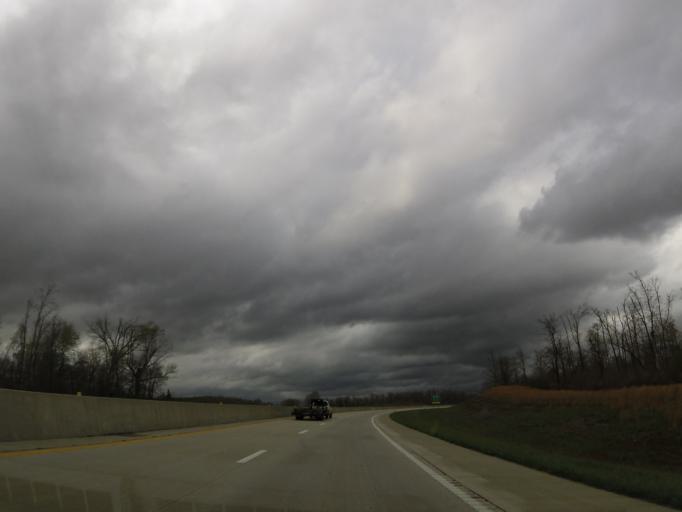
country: US
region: Missouri
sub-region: Butler County
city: Poplar Bluff
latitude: 36.6716
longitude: -90.4920
